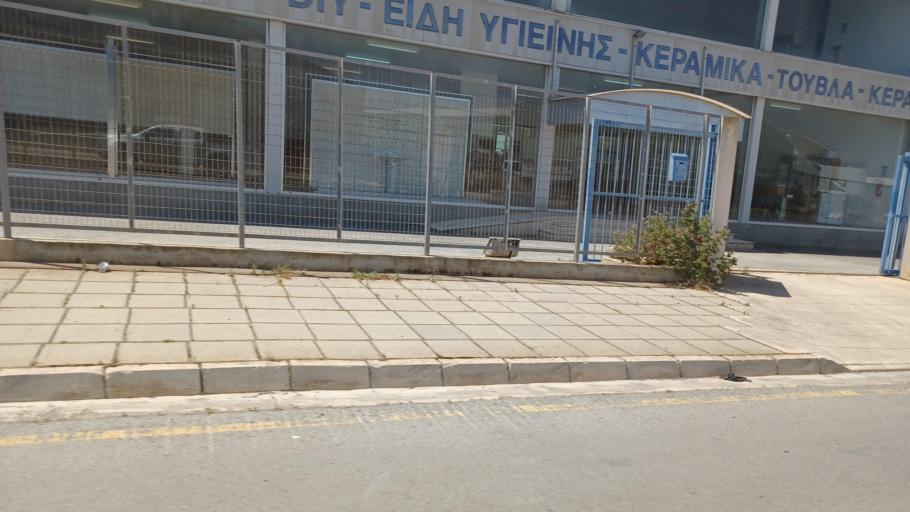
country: CY
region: Ammochostos
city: Frenaros
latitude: 35.0331
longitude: 33.9102
